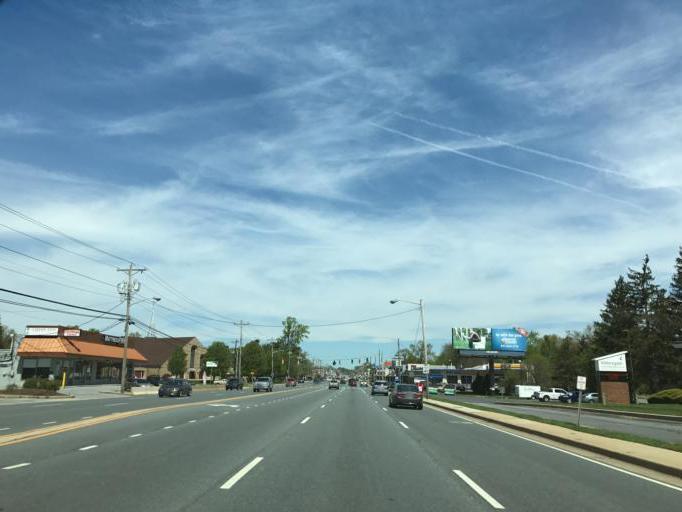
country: US
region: Delaware
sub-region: New Castle County
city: Bellefonte
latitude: 39.7926
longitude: -75.5468
